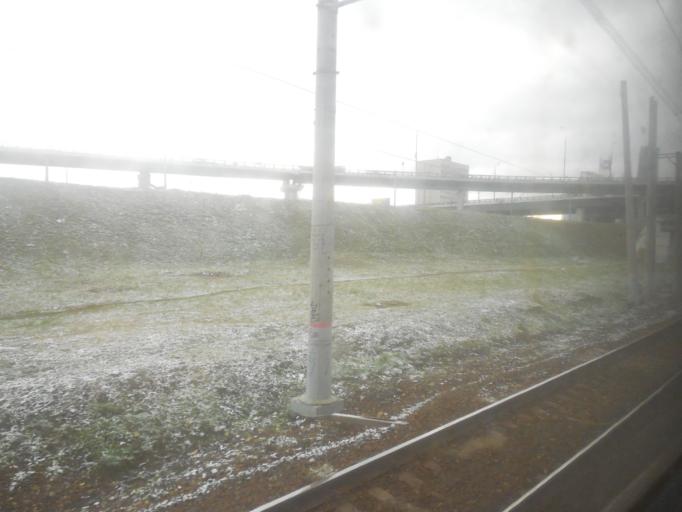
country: RU
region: Moskovskaya
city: Presnenskiy
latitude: 55.7679
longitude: 37.5363
